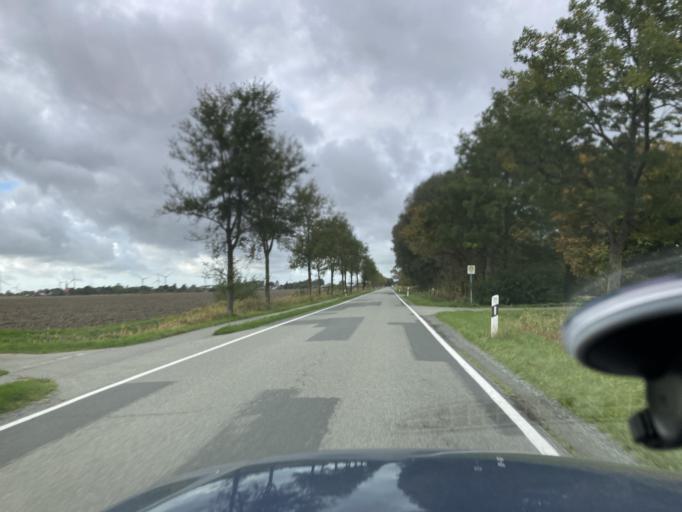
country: DE
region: Schleswig-Holstein
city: Neuenkirchen
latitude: 54.2322
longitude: 9.0111
